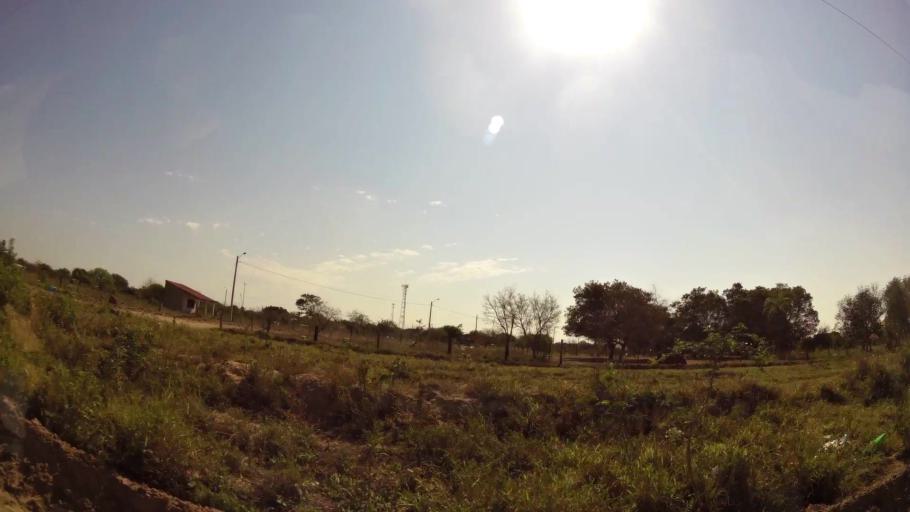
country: BO
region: Santa Cruz
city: Cotoca
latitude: -17.7311
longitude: -63.0726
